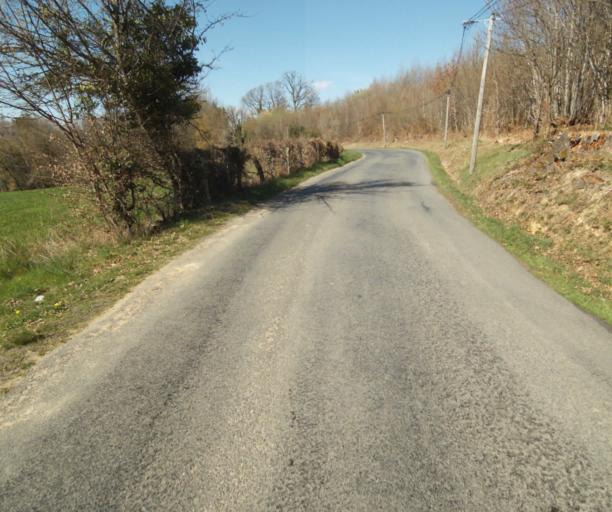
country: FR
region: Limousin
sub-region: Departement de la Correze
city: Saint-Mexant
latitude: 45.2947
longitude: 1.6853
